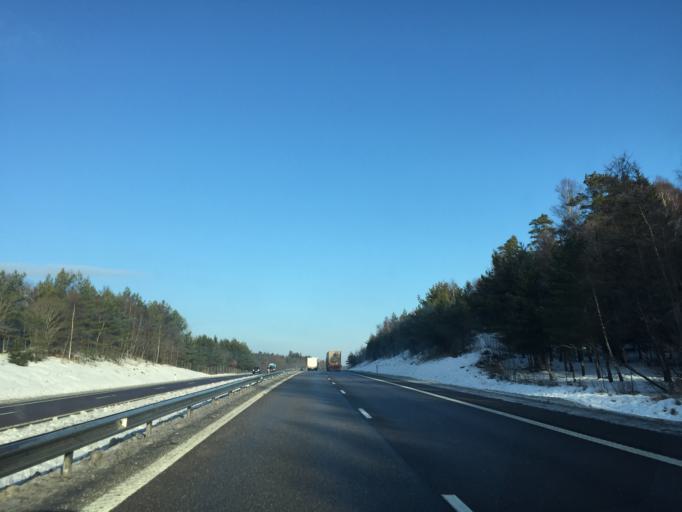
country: SE
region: Vaestra Goetaland
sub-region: Stenungsunds Kommun
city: Stenungsund
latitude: 58.0817
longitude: 11.8856
